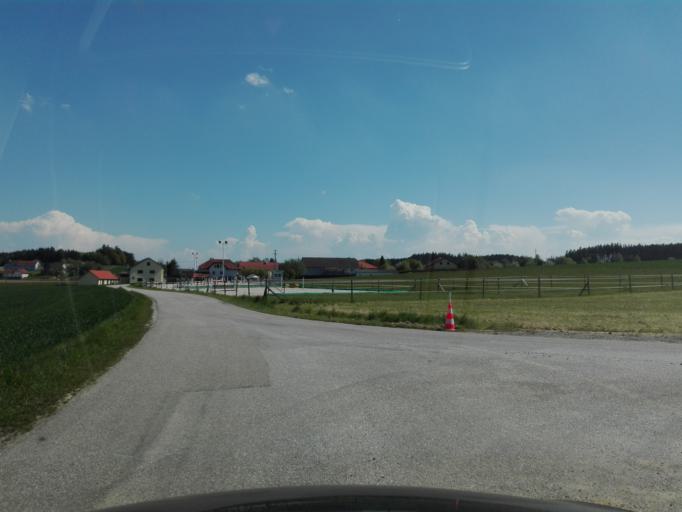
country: AT
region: Upper Austria
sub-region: Politischer Bezirk Grieskirchen
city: Bad Schallerbach
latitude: 48.3393
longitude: 13.8958
